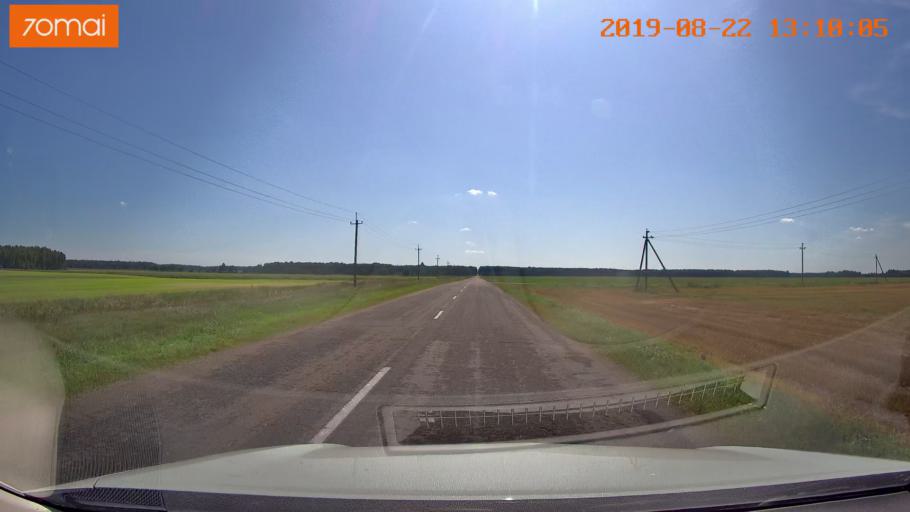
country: BY
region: Minsk
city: Prawdzinski
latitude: 53.3016
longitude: 27.8468
